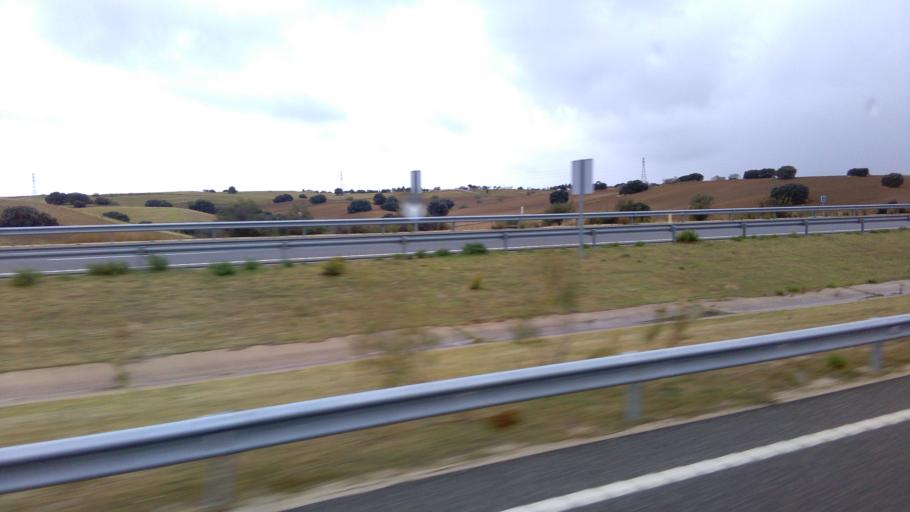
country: ES
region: Madrid
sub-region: Provincia de Madrid
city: Arroyomolinos
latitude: 40.2551
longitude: -3.9210
